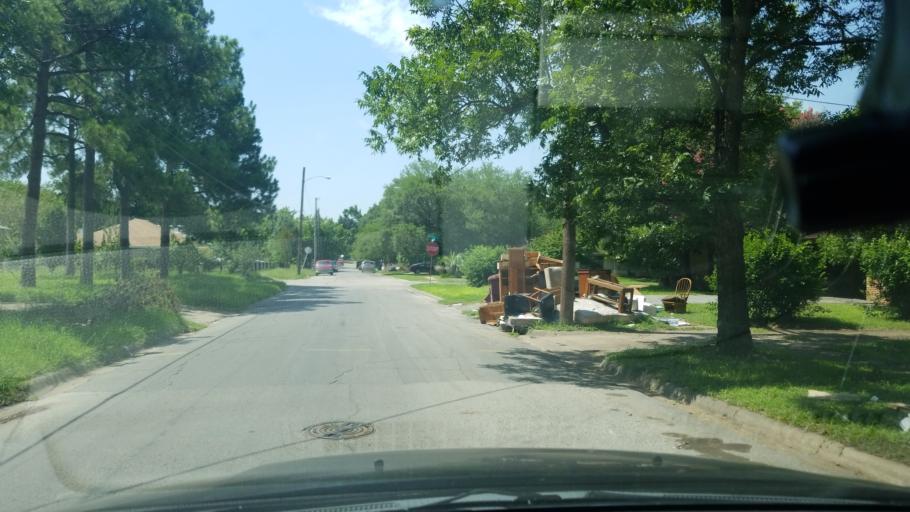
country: US
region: Texas
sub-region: Dallas County
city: Balch Springs
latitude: 32.7469
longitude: -96.6845
